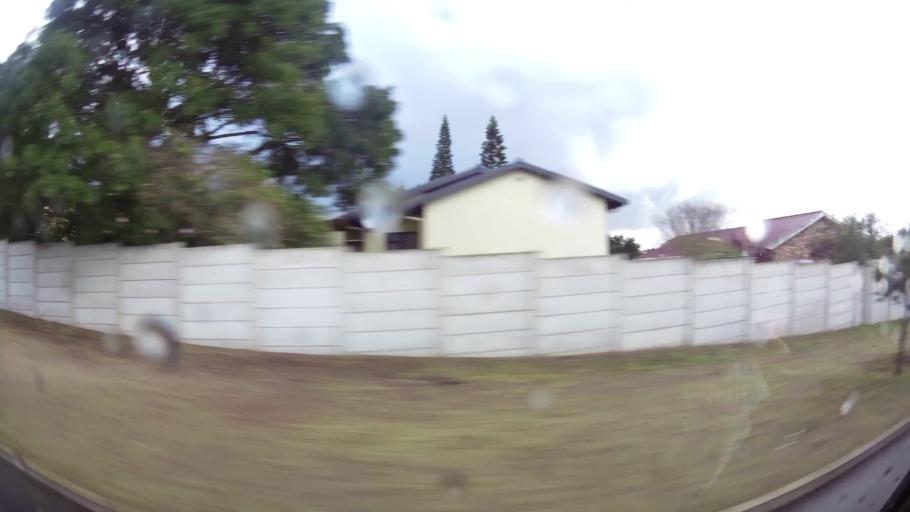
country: ZA
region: Western Cape
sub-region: Eden District Municipality
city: Mossel Bay
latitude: -34.1885
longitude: 22.1140
